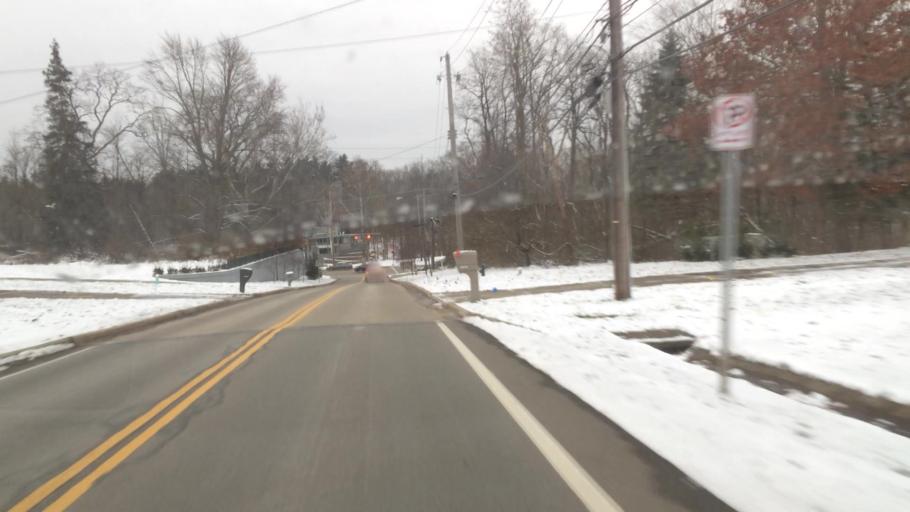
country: US
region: Ohio
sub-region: Cuyahoga County
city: Strongsville
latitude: 41.3147
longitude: -81.7910
